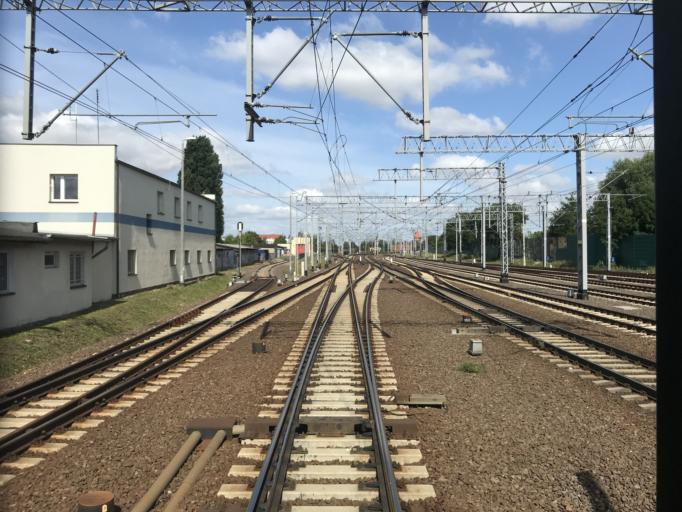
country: PL
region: Pomeranian Voivodeship
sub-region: Powiat malborski
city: Malbork
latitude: 54.0380
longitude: 19.0389
